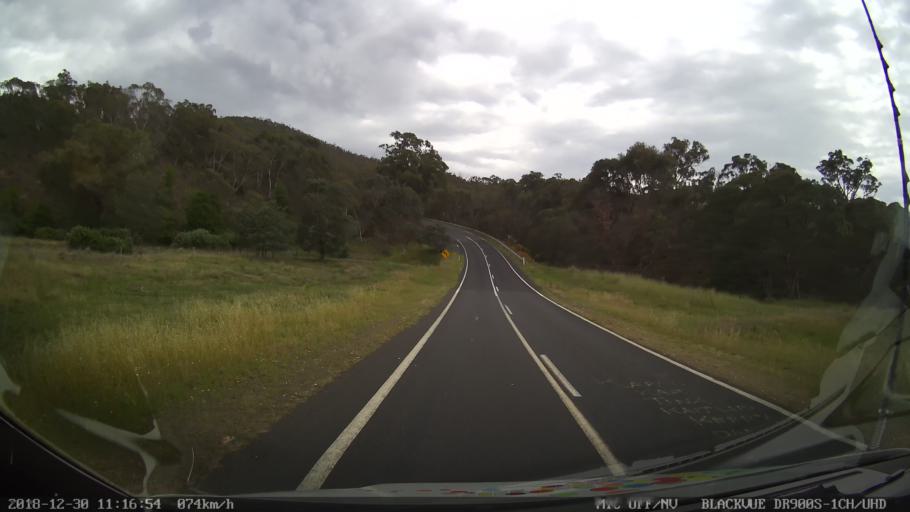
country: AU
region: New South Wales
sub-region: Snowy River
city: Jindabyne
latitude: -36.5380
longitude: 148.7023
